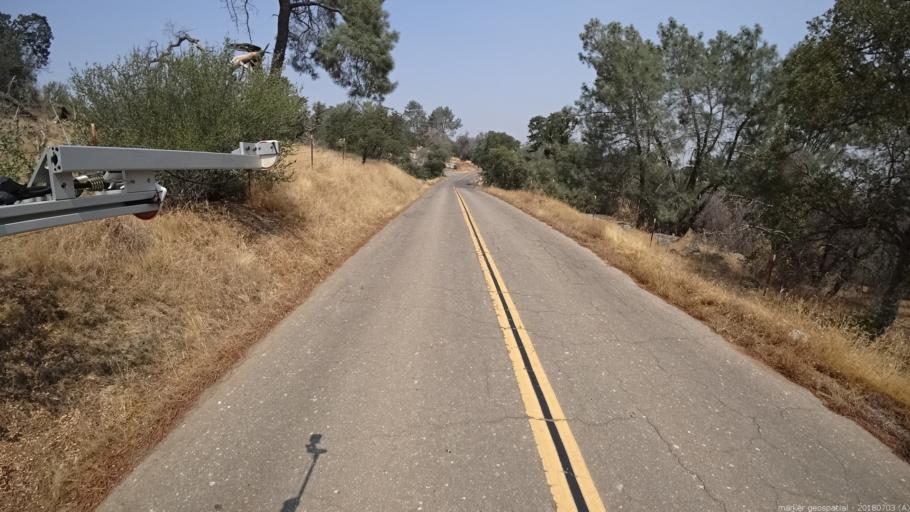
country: US
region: California
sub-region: Madera County
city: Yosemite Lakes
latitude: 37.0630
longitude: -119.6683
